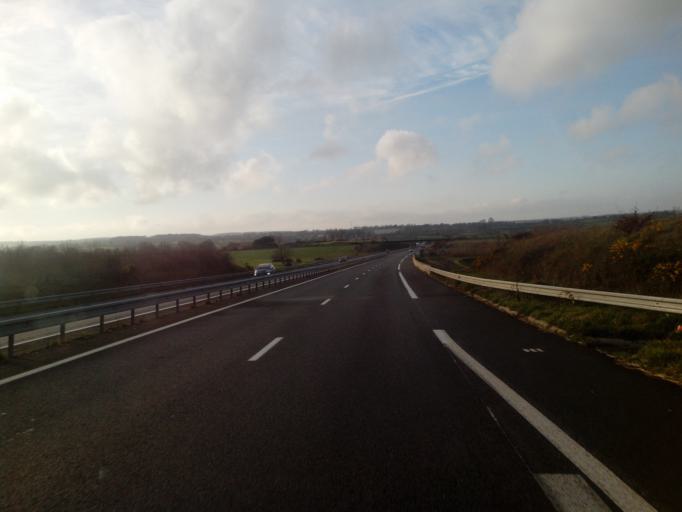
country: FR
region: Poitou-Charentes
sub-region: Departement des Deux-Sevres
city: Le Pin
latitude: 46.8975
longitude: -0.6396
